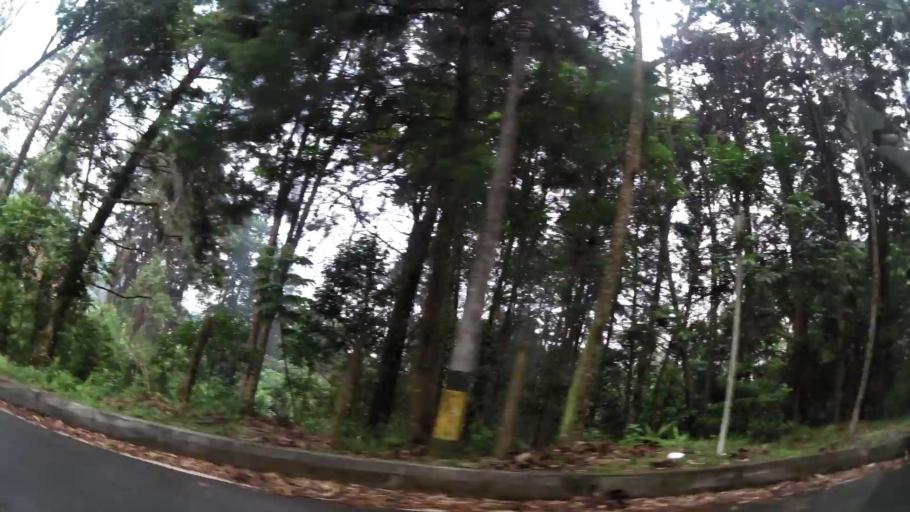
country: CO
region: Antioquia
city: Medellin
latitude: 6.2043
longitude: -75.5454
